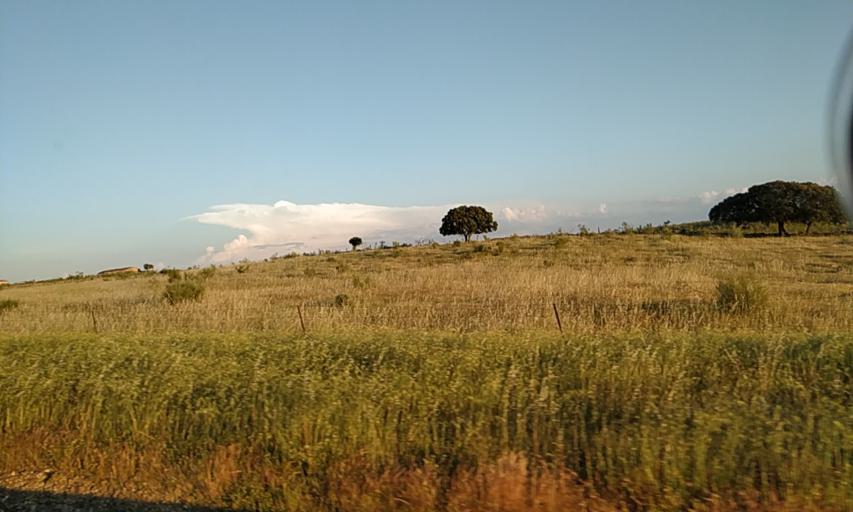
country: ES
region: Extremadura
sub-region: Provincia de Caceres
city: Salorino
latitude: 39.5145
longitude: -7.0580
